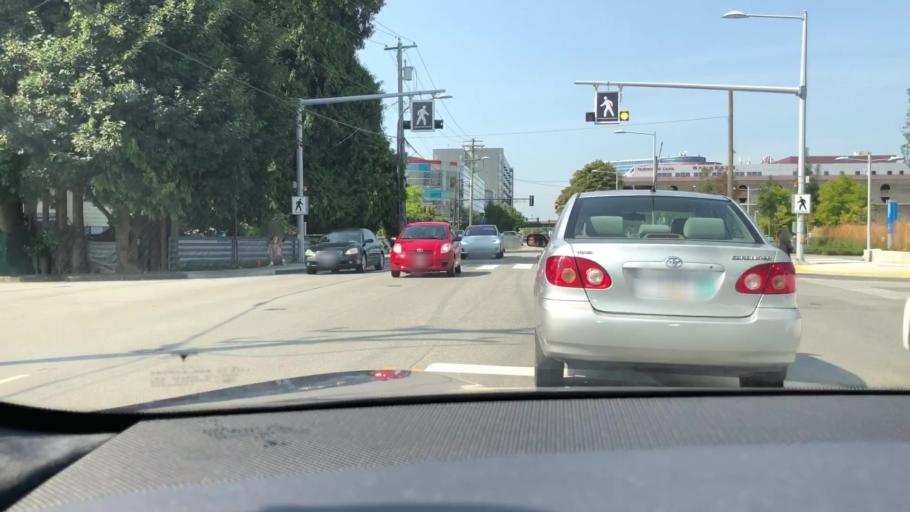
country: CA
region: British Columbia
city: Richmond
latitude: 49.1847
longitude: -123.1307
